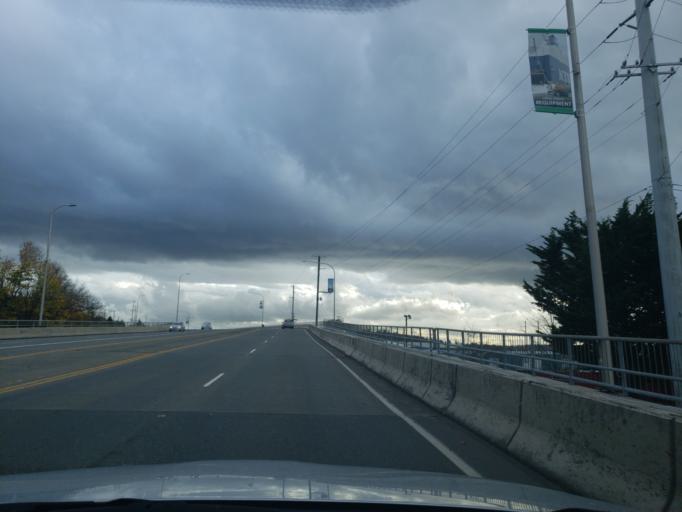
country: US
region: Washington
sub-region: Snohomish County
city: Everett
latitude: 47.9904
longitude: -122.2141
